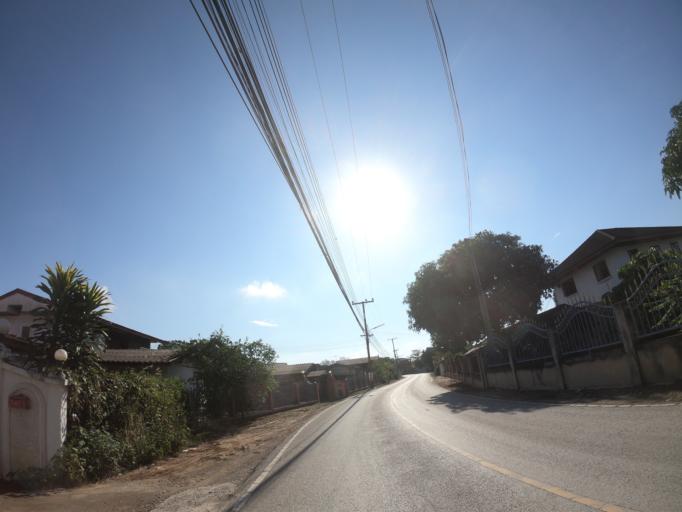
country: TH
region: Chiang Mai
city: Saraphi
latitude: 18.6953
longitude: 98.9975
